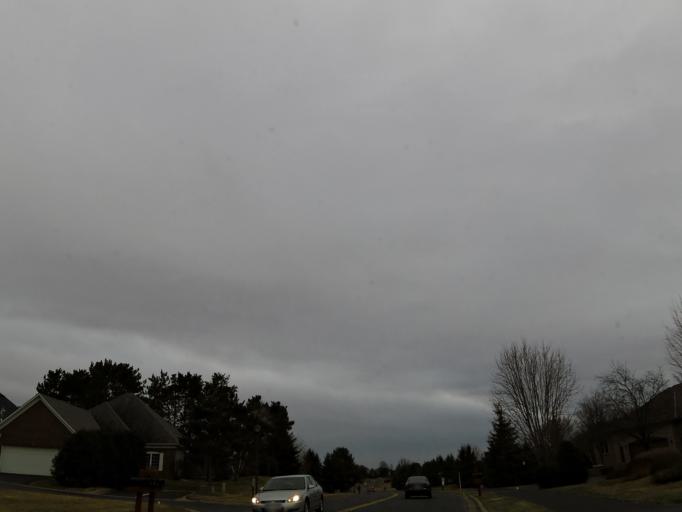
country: US
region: Wisconsin
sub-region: Saint Croix County
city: Hudson
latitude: 44.9770
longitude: -92.7305
